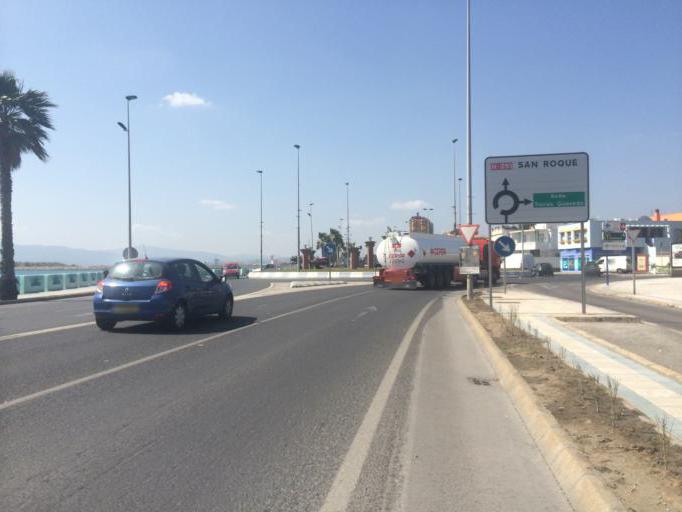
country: ES
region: Andalusia
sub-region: Provincia de Cadiz
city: La Linea de la Concepcion
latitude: 36.1666
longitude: -5.3639
